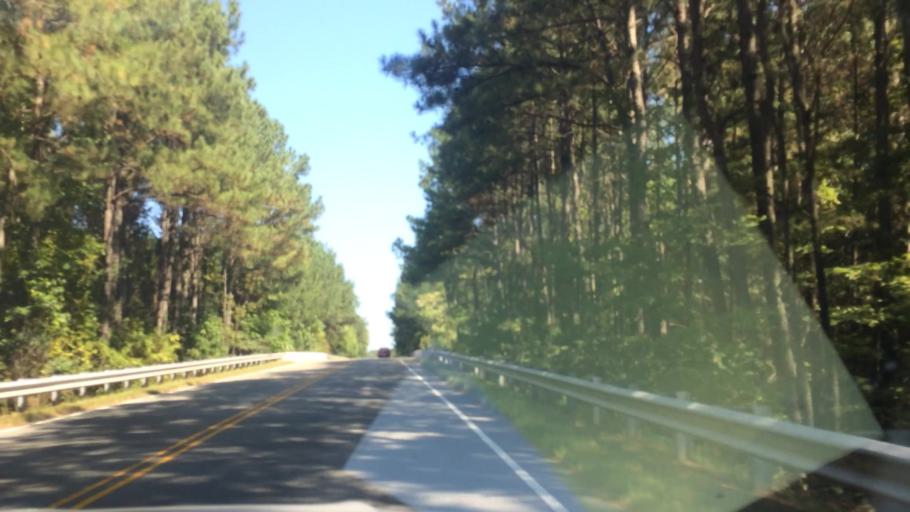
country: US
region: Virginia
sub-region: James City County
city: Williamsburg
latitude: 37.3759
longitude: -76.7745
